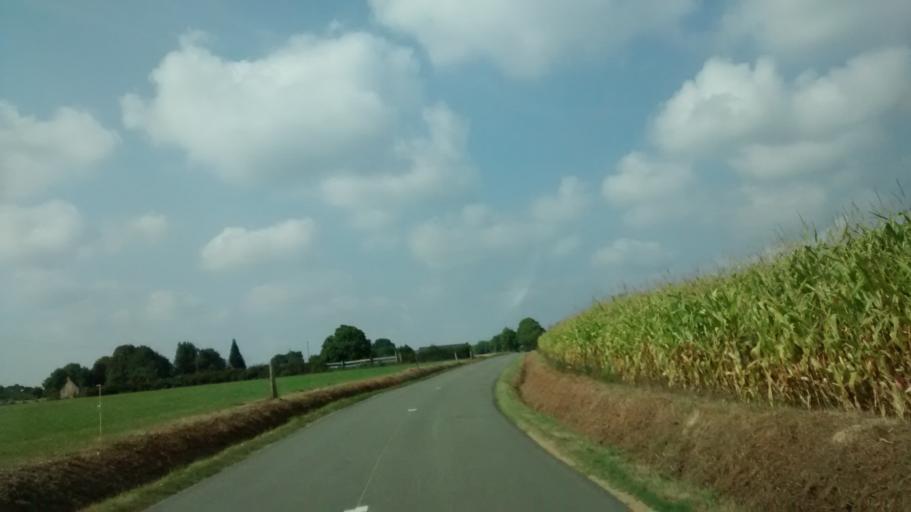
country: FR
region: Brittany
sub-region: Departement d'Ille-et-Vilaine
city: Chatillon-en-Vendelais
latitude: 48.2263
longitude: -1.2358
